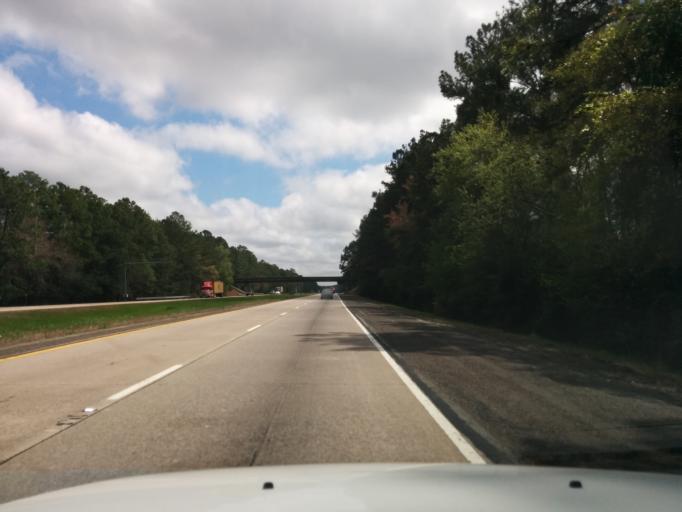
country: US
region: Georgia
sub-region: Chatham County
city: Bloomingdale
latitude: 32.1615
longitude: -81.4349
